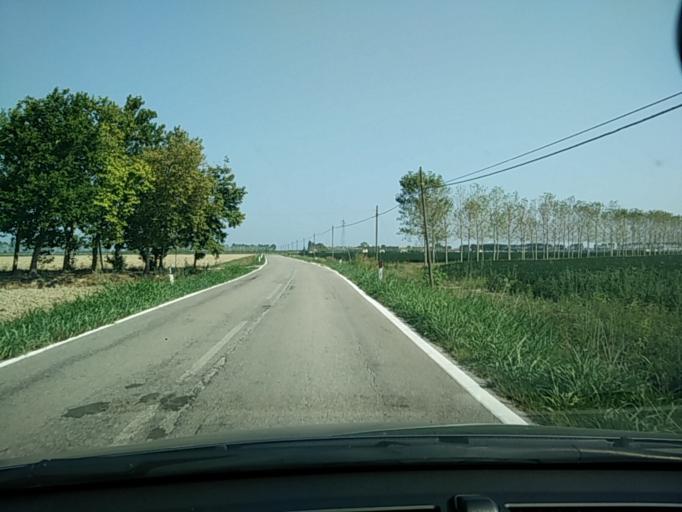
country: IT
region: Veneto
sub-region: Provincia di Venezia
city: Caorle
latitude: 45.6212
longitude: 12.8488
